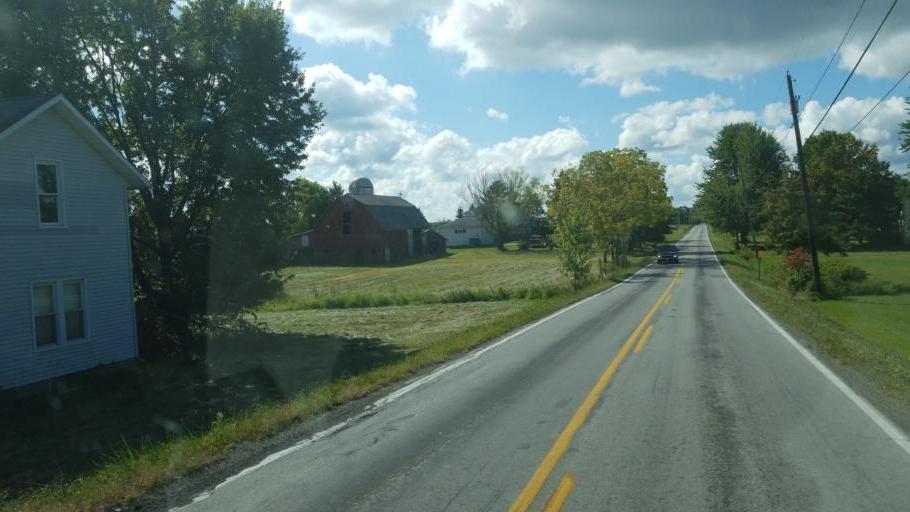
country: US
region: Ohio
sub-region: Lorain County
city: Lagrange
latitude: 41.2216
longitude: -82.1393
